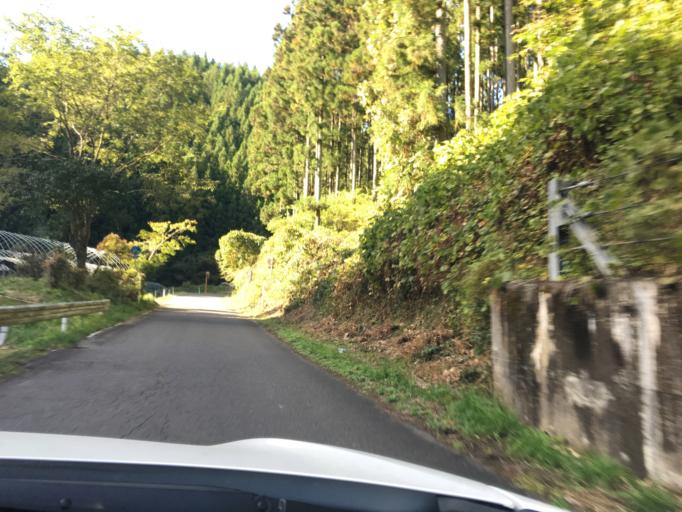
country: JP
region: Fukushima
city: Ishikawa
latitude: 37.1250
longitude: 140.5562
